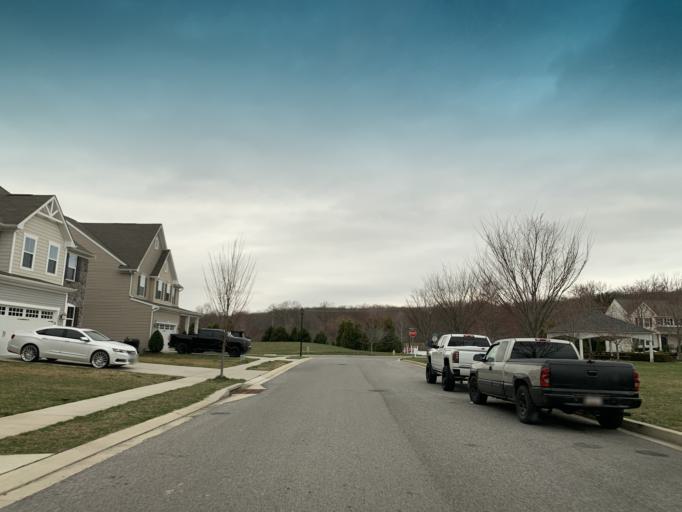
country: US
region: Maryland
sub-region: Harford County
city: Aberdeen
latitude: 39.5420
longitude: -76.1947
